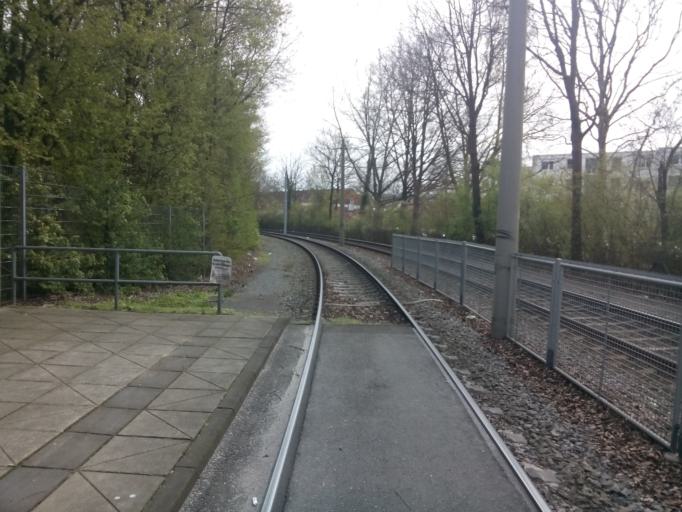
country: DE
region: Bremen
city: Bremen
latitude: 53.0372
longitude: 8.8228
